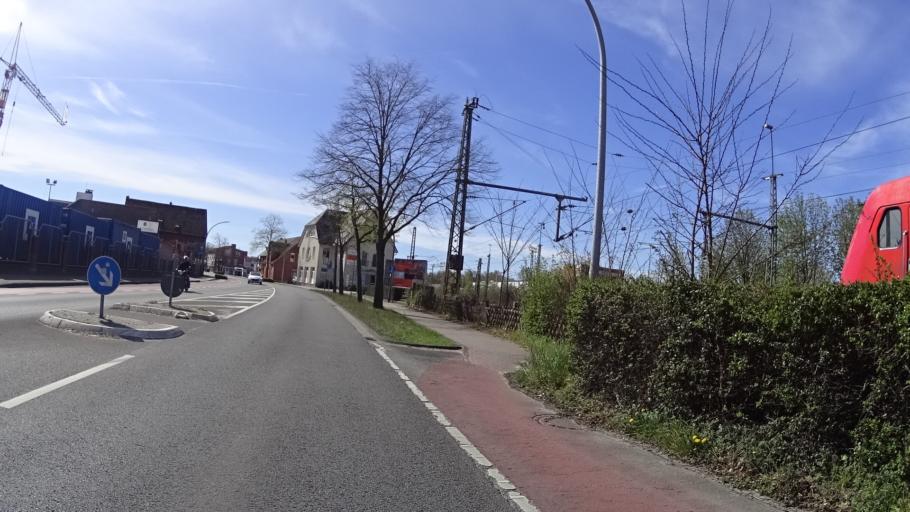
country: DE
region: Lower Saxony
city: Lingen
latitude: 52.5151
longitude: 7.3186
